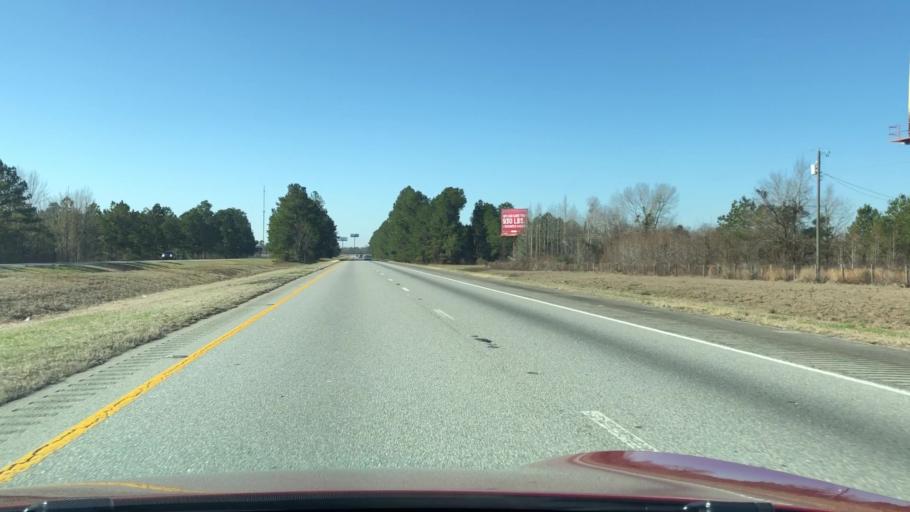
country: US
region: South Carolina
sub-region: Clarendon County
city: Manning
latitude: 33.6079
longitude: -80.3195
